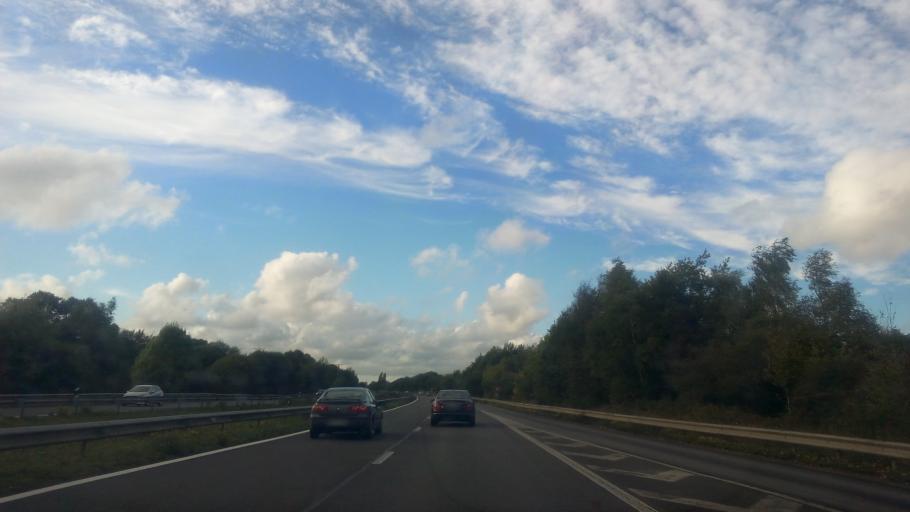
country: FR
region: Pays de la Loire
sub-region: Departement de la Loire-Atlantique
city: Le Temple-de-Bretagne
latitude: 47.3301
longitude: -1.7852
